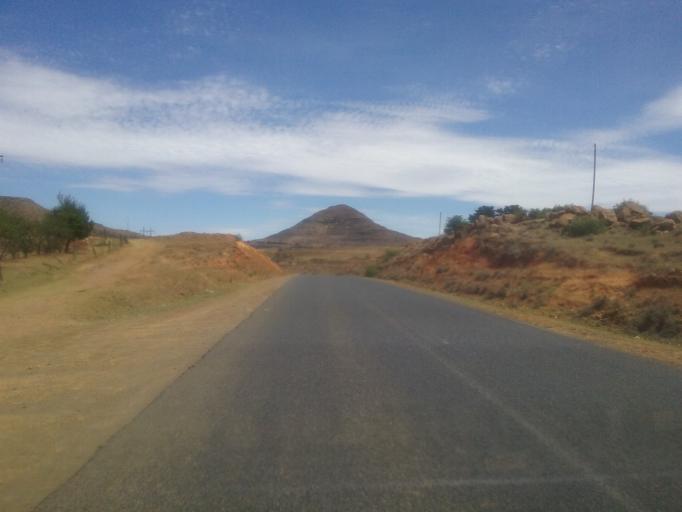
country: LS
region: Mafeteng
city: Mafeteng
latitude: -29.9665
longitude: 27.3038
